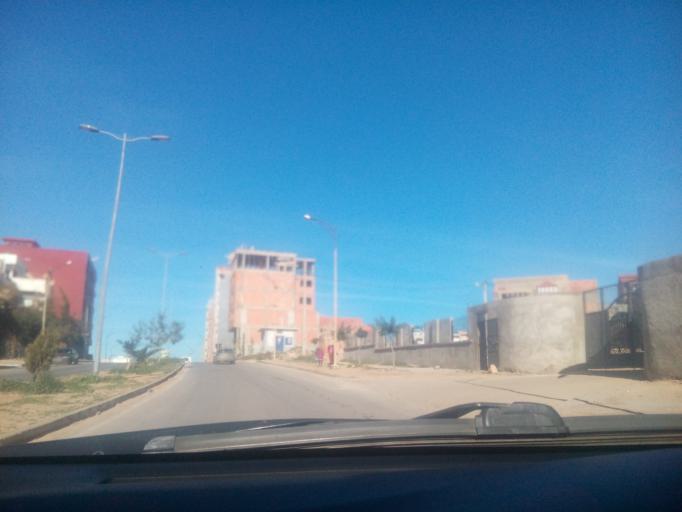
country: DZ
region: Oran
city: Bir el Djir
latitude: 35.7487
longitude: -0.5506
